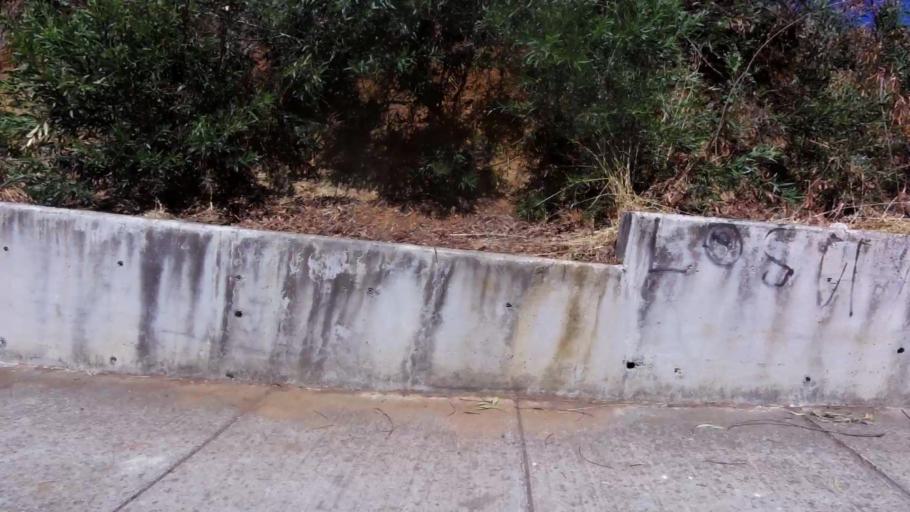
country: CL
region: Biobio
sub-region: Provincia de Concepcion
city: Penco
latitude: -36.7374
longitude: -72.9857
